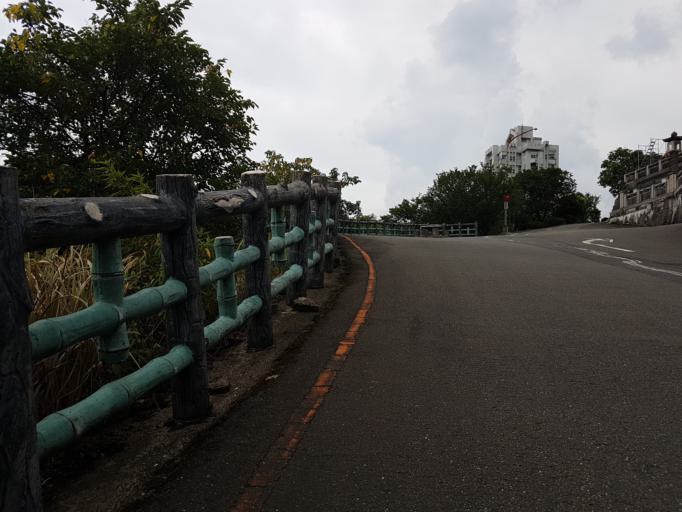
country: TW
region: Taiwan
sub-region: Keelung
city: Keelung
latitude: 25.0546
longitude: 121.6648
